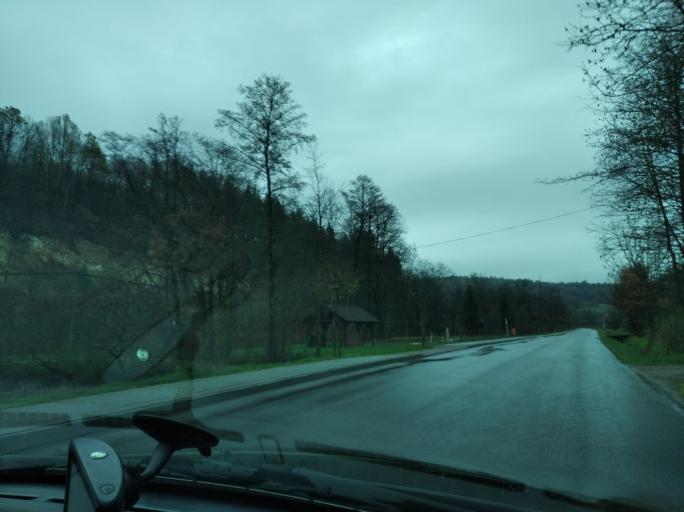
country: PL
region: Subcarpathian Voivodeship
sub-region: Powiat rzeszowski
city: Straszydle
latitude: 49.9015
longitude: 22.0037
